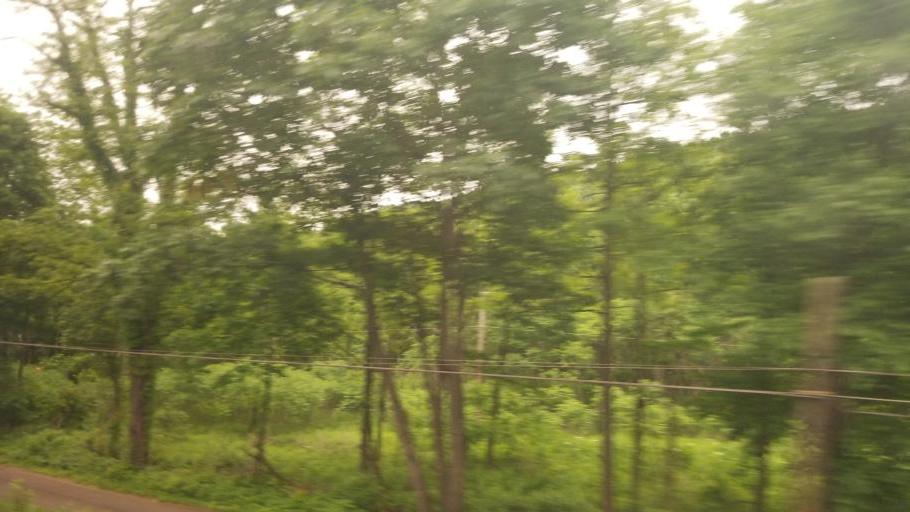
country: US
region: Pennsylvania
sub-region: Somerset County
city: Milford
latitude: 39.8861
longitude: -79.2066
